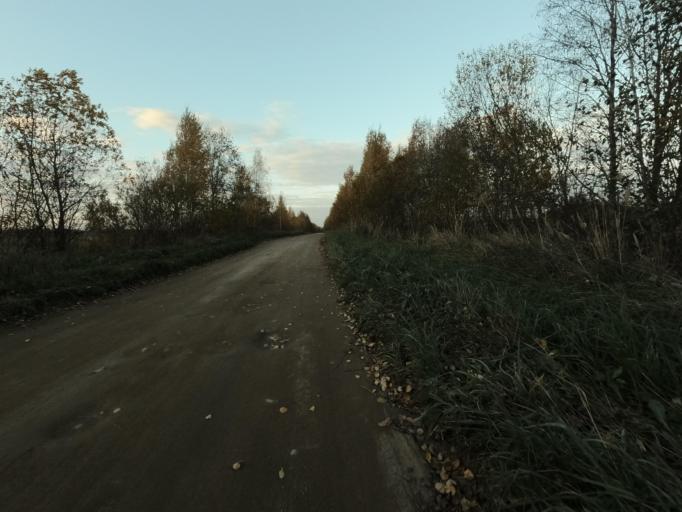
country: RU
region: Leningrad
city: Mga
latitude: 59.7995
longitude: 31.2003
